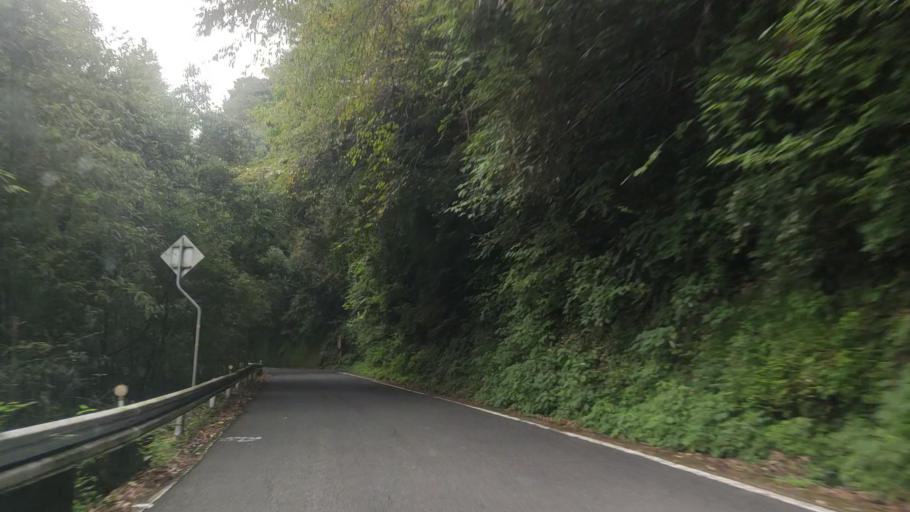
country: JP
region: Wakayama
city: Koya
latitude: 34.2506
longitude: 135.5451
